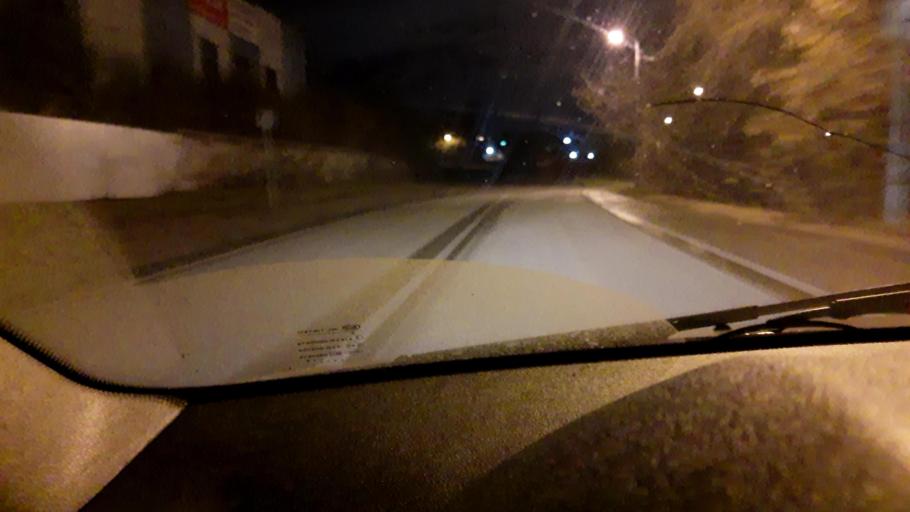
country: RU
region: Bashkortostan
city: Ufa
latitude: 54.8605
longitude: 56.0759
